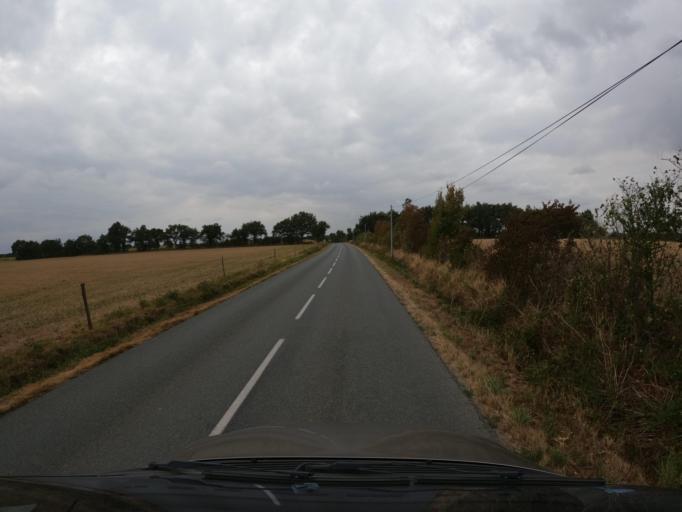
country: FR
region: Pays de la Loire
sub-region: Departement de la Vendee
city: Tiffauges
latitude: 46.9917
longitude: -1.0880
